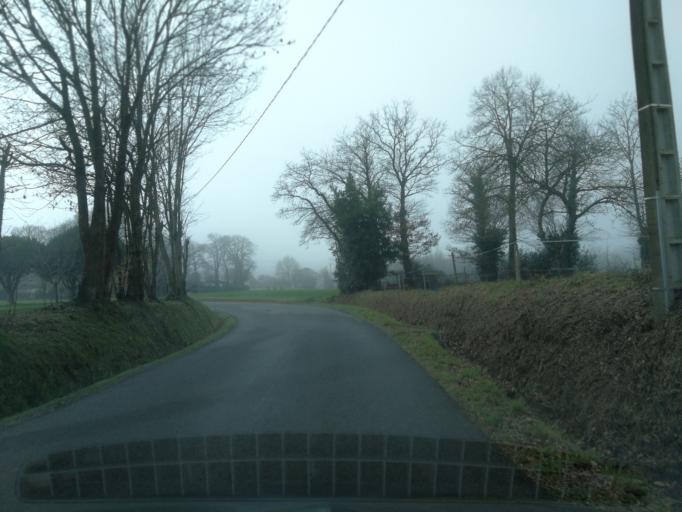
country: FR
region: Brittany
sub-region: Departement du Morbihan
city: La Vraie-Croix
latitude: 47.7358
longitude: -2.5039
